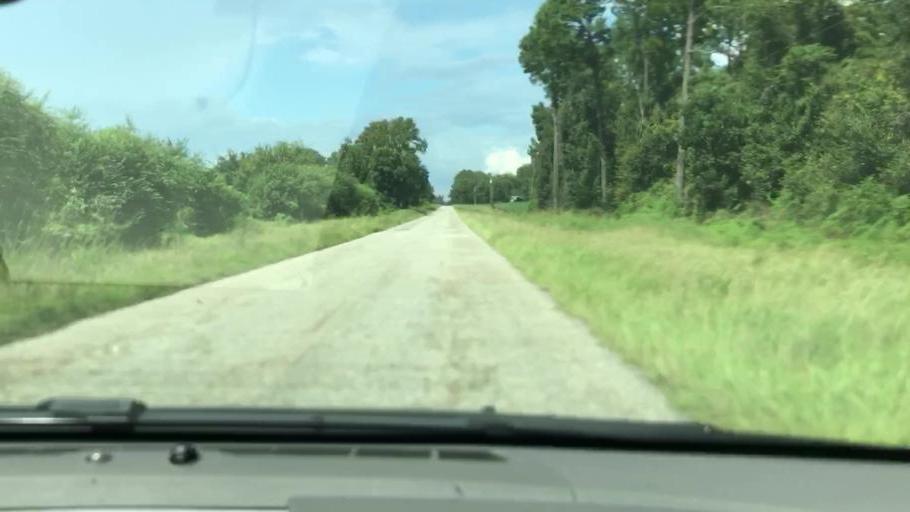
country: US
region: Georgia
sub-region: Early County
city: Blakely
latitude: 31.2038
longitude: -85.0036
